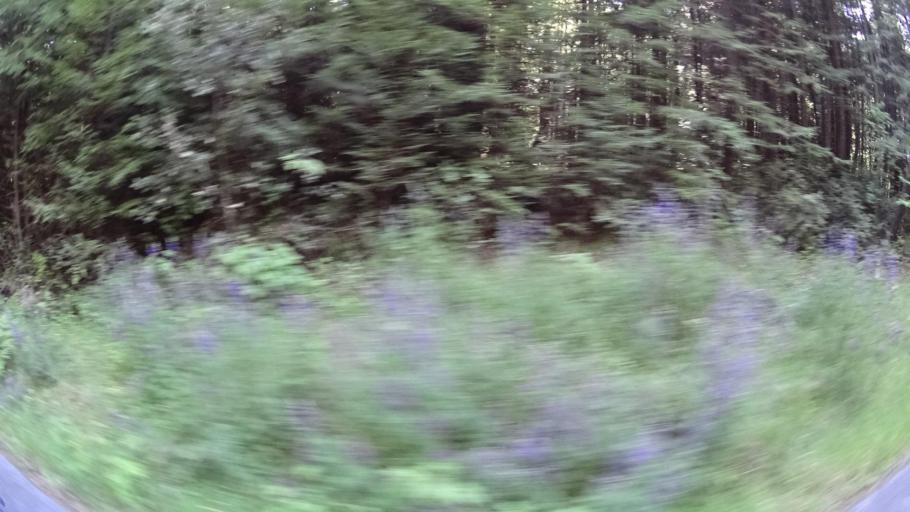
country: US
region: California
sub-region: Humboldt County
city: Rio Dell
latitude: 40.4384
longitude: -123.9701
